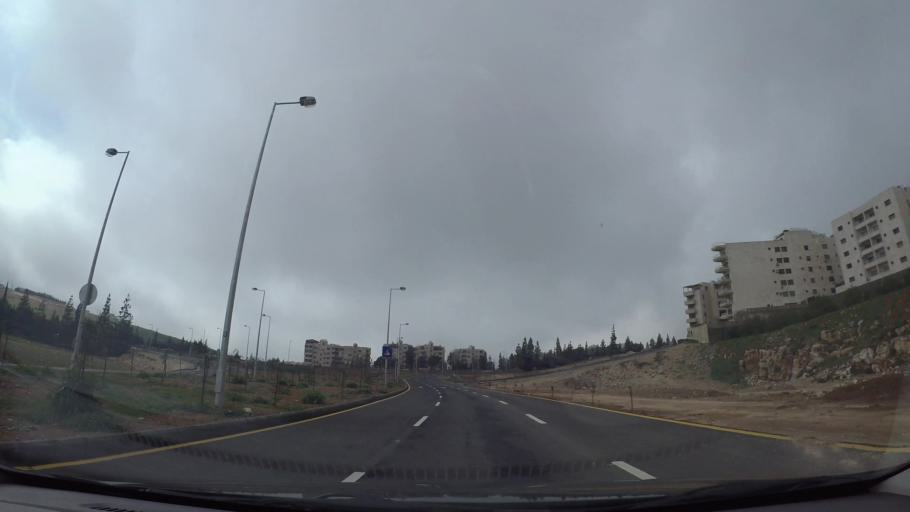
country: JO
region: Amman
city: Wadi as Sir
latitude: 31.9365
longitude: 35.8562
